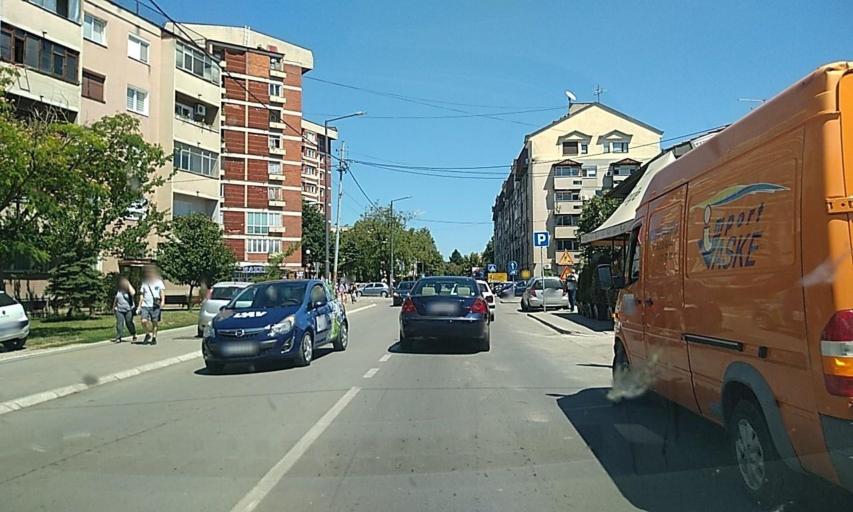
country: RS
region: Central Serbia
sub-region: Branicevski Okrug
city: Pozarevac
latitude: 44.6122
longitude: 21.1762
